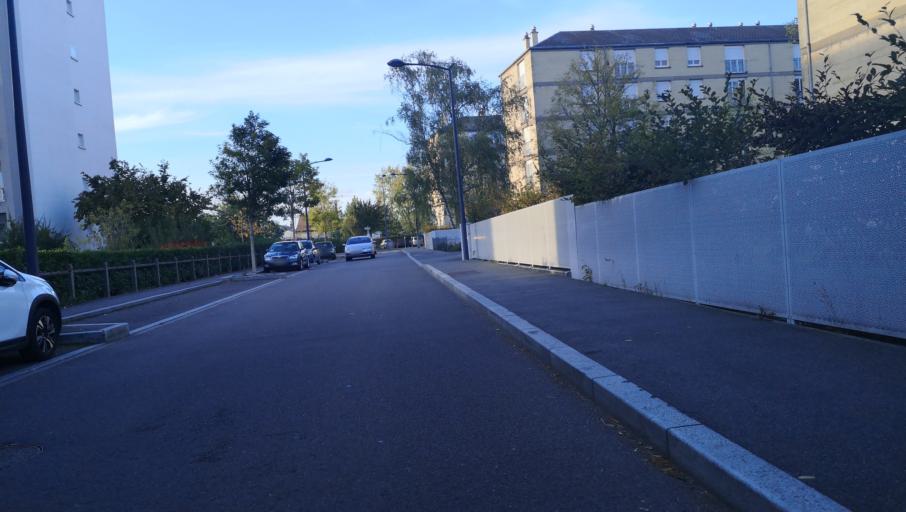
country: FR
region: Centre
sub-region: Departement du Loiret
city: Saint-Jean-de-la-Ruelle
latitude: 47.9003
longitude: 1.8780
